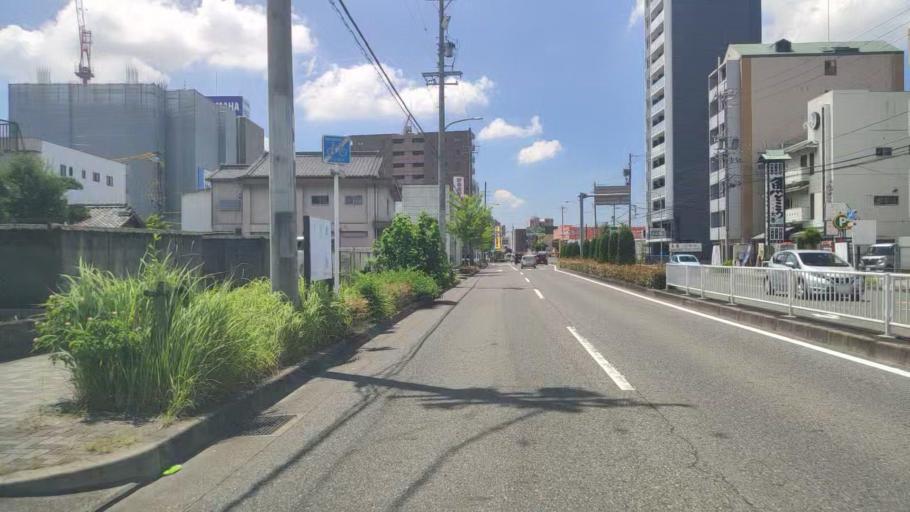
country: JP
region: Aichi
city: Kanie
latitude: 35.1480
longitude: 136.8533
